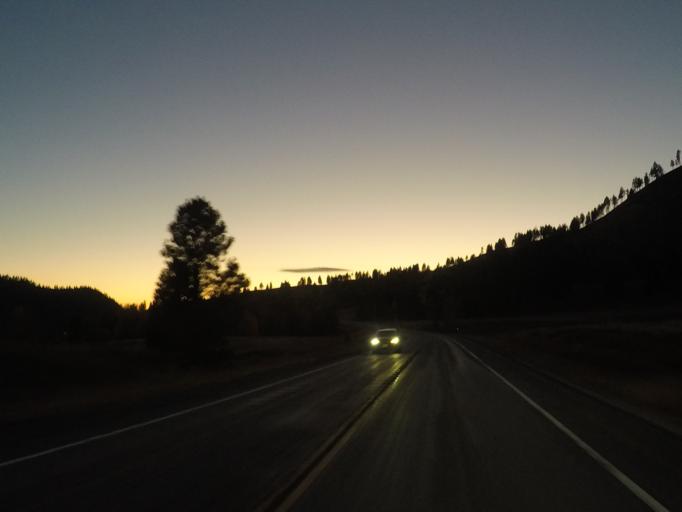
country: US
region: Montana
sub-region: Missoula County
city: Seeley Lake
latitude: 47.0302
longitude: -113.2762
